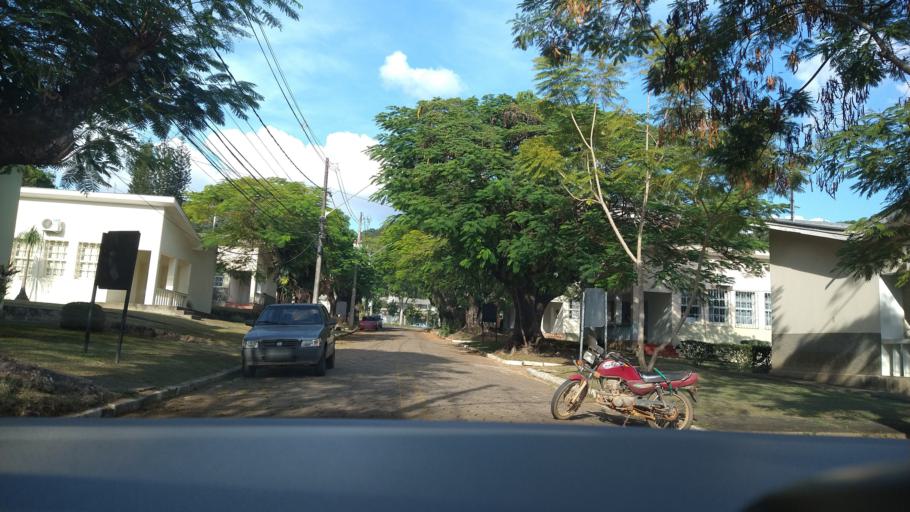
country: BR
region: Minas Gerais
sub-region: Vicosa
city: Vicosa
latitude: -20.7543
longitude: -42.8745
